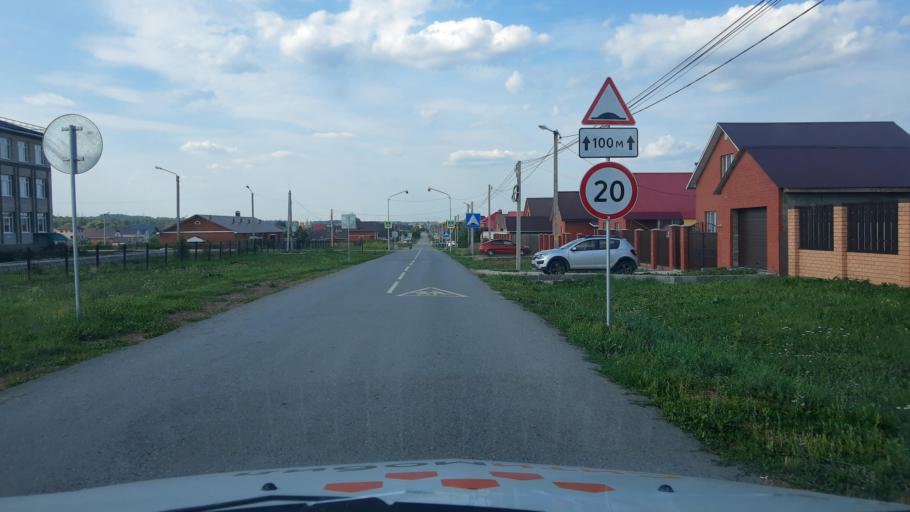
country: RU
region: Bashkortostan
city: Kabakovo
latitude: 54.6560
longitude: 56.2126
